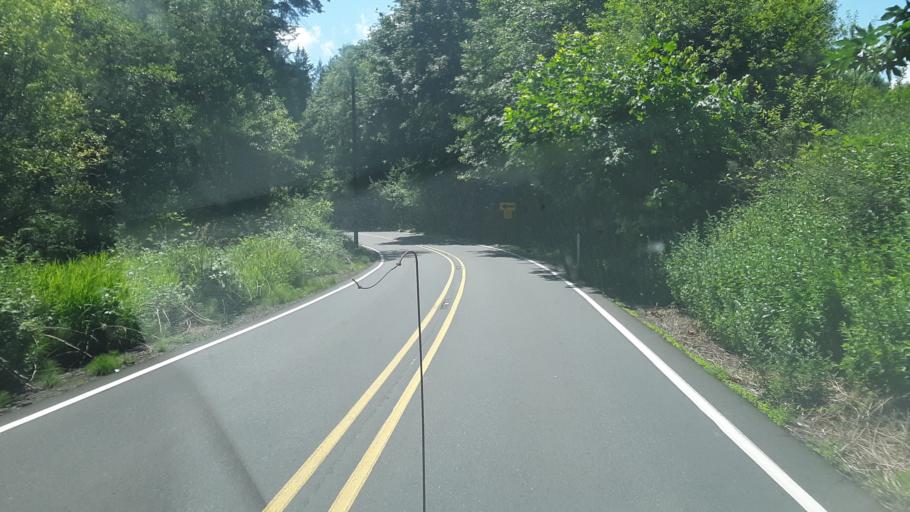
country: US
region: Washington
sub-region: Clark County
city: Amboy
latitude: 45.9369
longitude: -122.3798
